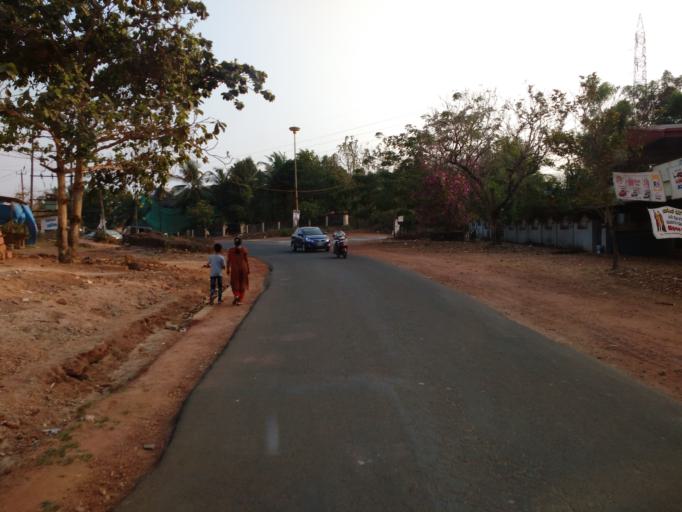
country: IN
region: Karnataka
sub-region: Dakshina Kannada
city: Mangalore
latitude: 12.9201
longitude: 74.8981
